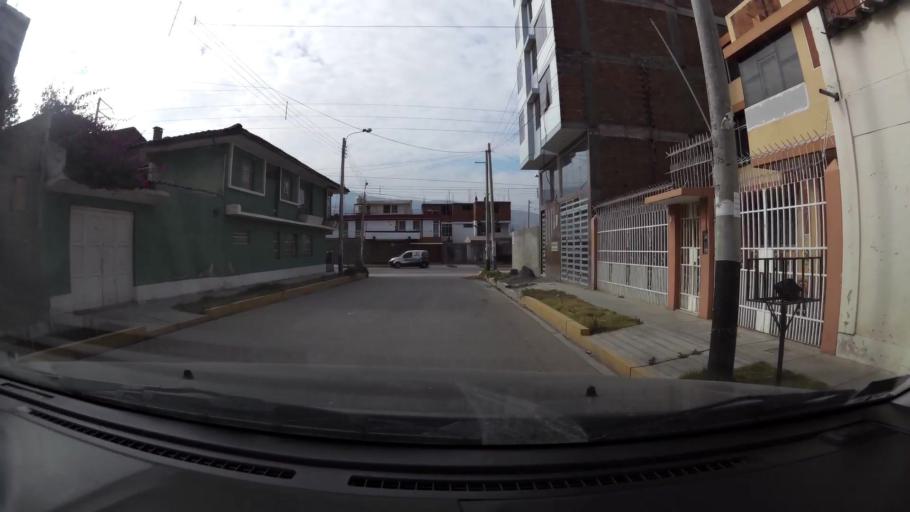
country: PE
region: Junin
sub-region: Provincia de Huancayo
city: Huancayo
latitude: -12.0566
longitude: -75.2035
